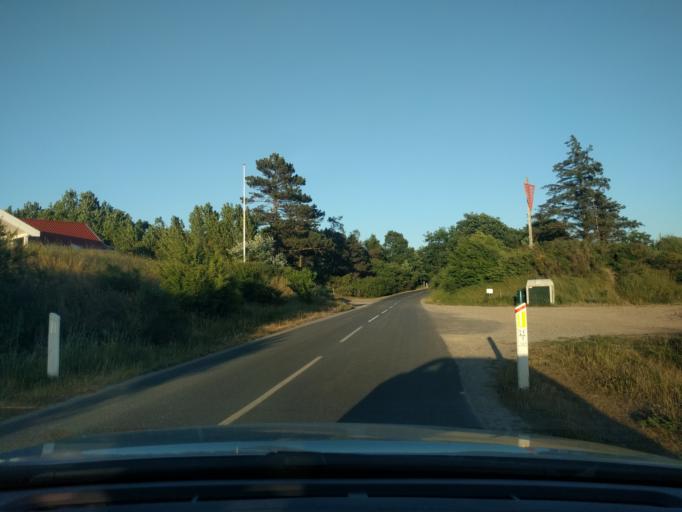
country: DK
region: South Denmark
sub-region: Kerteminde Kommune
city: Munkebo
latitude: 55.6086
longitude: 10.6163
